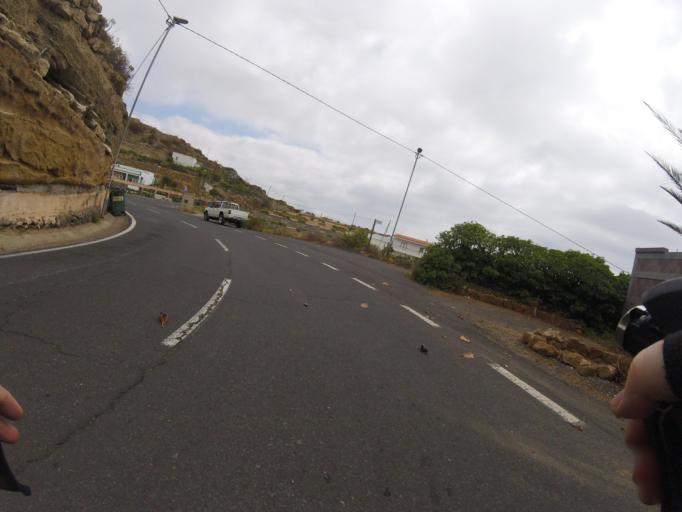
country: ES
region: Canary Islands
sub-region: Provincia de Santa Cruz de Tenerife
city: Guimar
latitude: 28.2773
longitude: -16.4116
